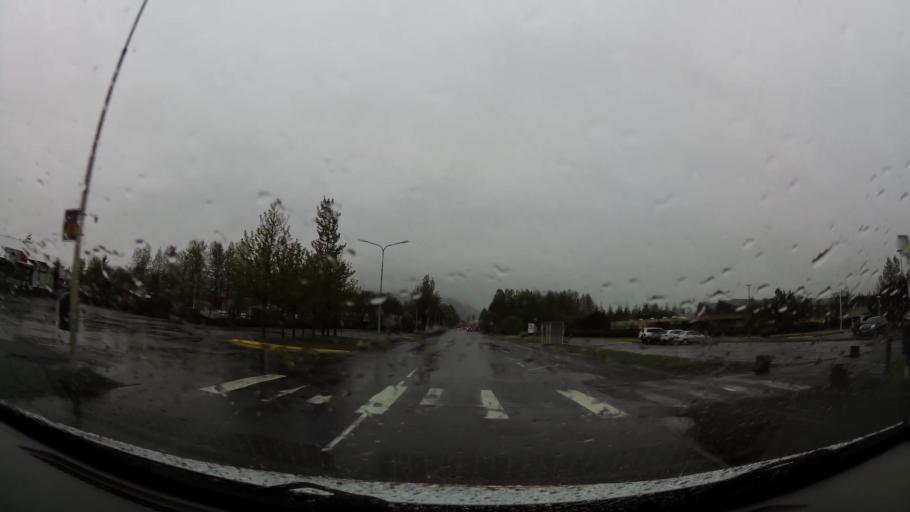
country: IS
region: South
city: Selfoss
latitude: 63.9323
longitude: -20.9992
